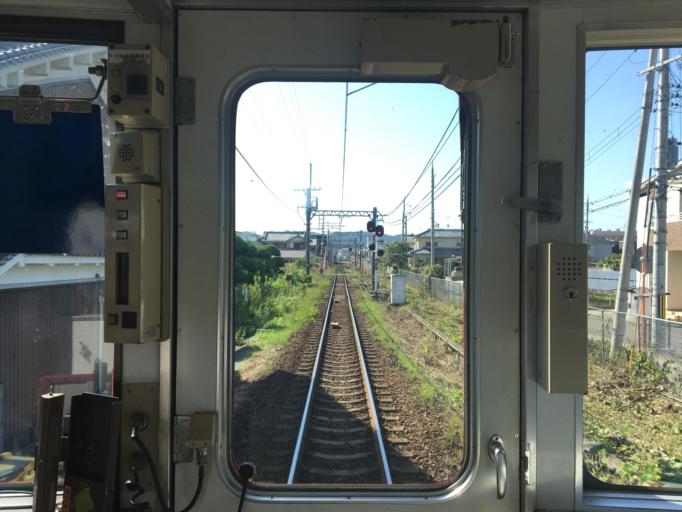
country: JP
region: Nara
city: Gose
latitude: 34.4671
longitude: 135.7324
